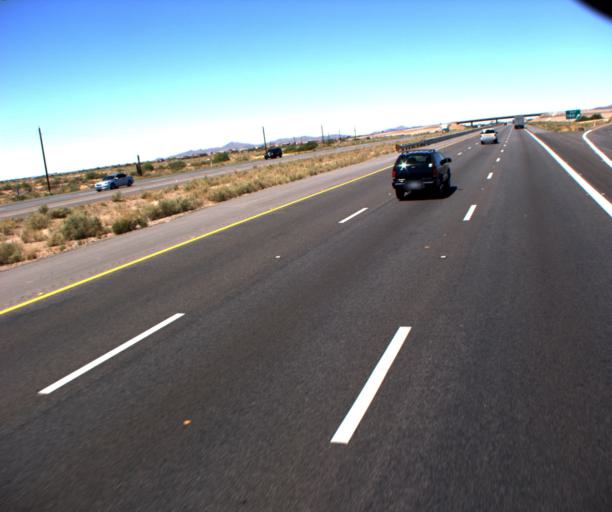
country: US
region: Arizona
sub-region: Pinal County
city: Casa Grande
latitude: 32.9339
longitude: -111.6971
